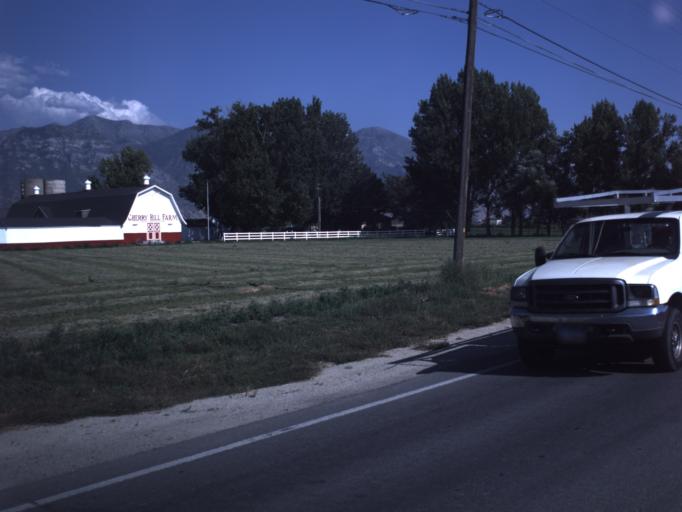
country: US
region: Utah
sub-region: Utah County
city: Orem
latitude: 40.2649
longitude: -111.7192
